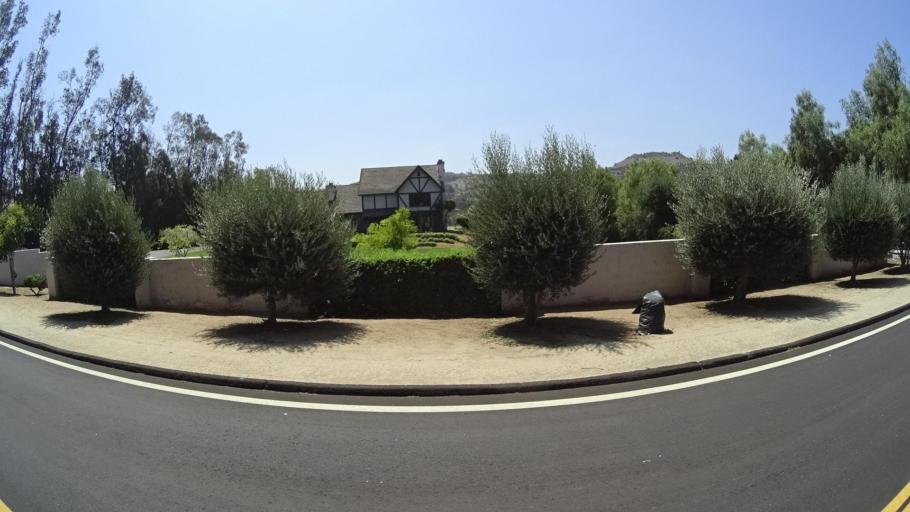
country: US
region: California
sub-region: San Diego County
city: Bonsall
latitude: 33.2820
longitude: -117.1891
